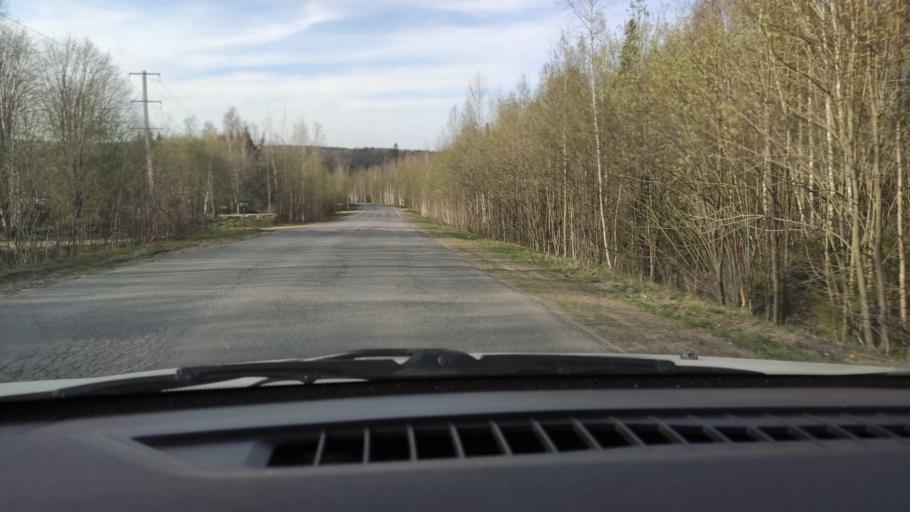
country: RU
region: Perm
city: Novyye Lyady
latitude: 57.9499
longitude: 56.5689
